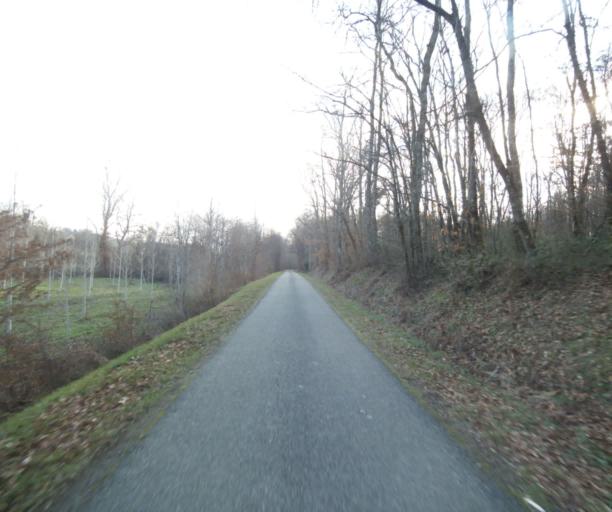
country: FR
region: Midi-Pyrenees
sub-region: Departement du Tarn-et-Garonne
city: Moissac
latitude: 44.1257
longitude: 1.0435
